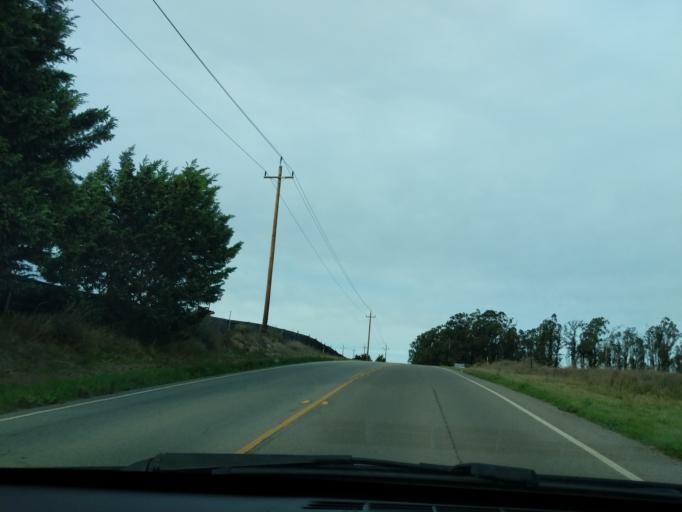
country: US
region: California
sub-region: San Luis Obispo County
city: Callender
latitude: 35.0187
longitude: -120.5643
